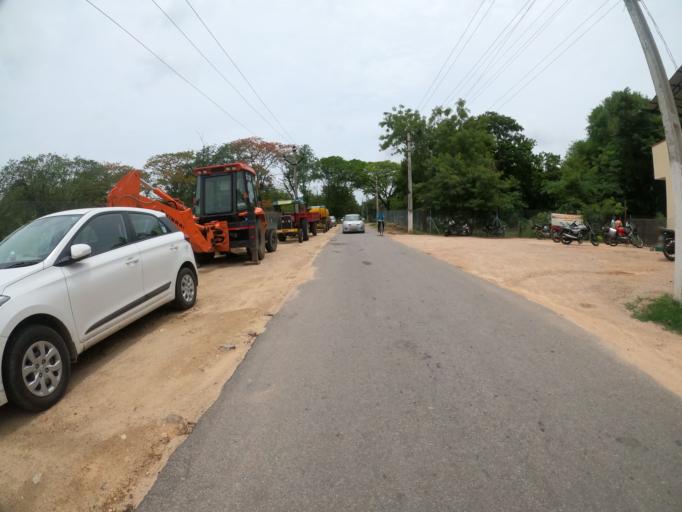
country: IN
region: Telangana
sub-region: Hyderabad
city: Hyderabad
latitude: 17.3391
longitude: 78.3625
